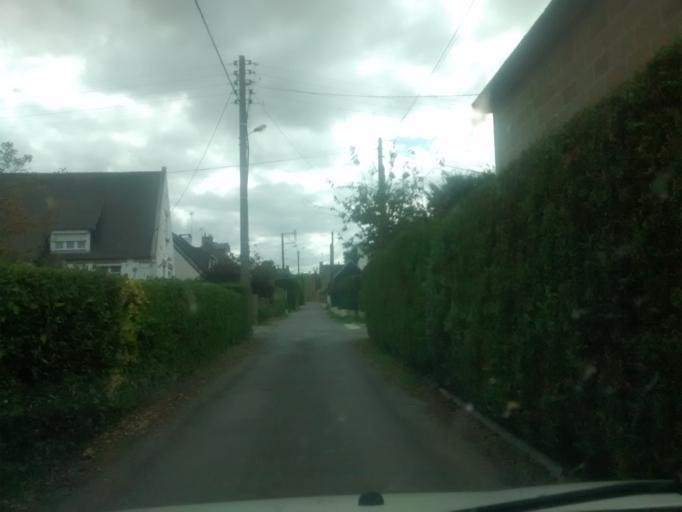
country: FR
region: Brittany
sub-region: Departement d'Ille-et-Vilaine
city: Saint-Briac-sur-Mer
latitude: 48.6240
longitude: -2.1346
